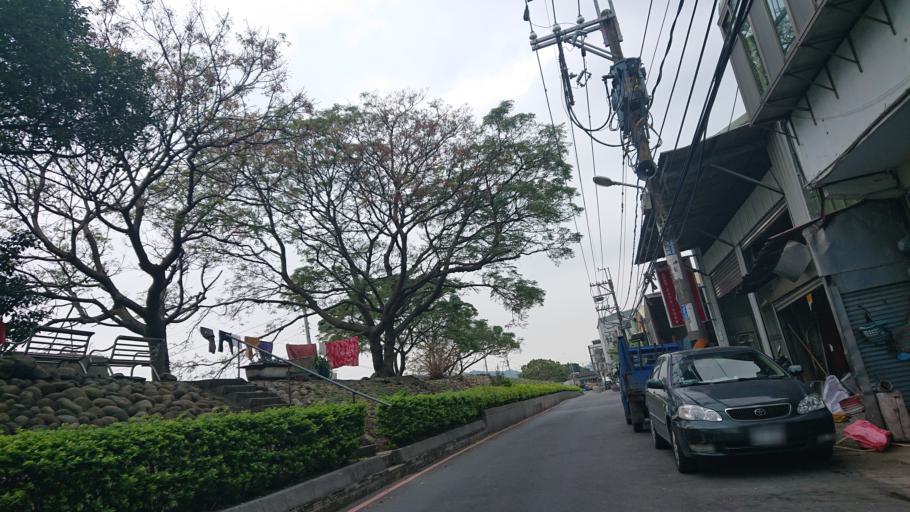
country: TW
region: Taiwan
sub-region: Taoyuan
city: Taoyuan
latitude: 24.9398
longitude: 121.3541
